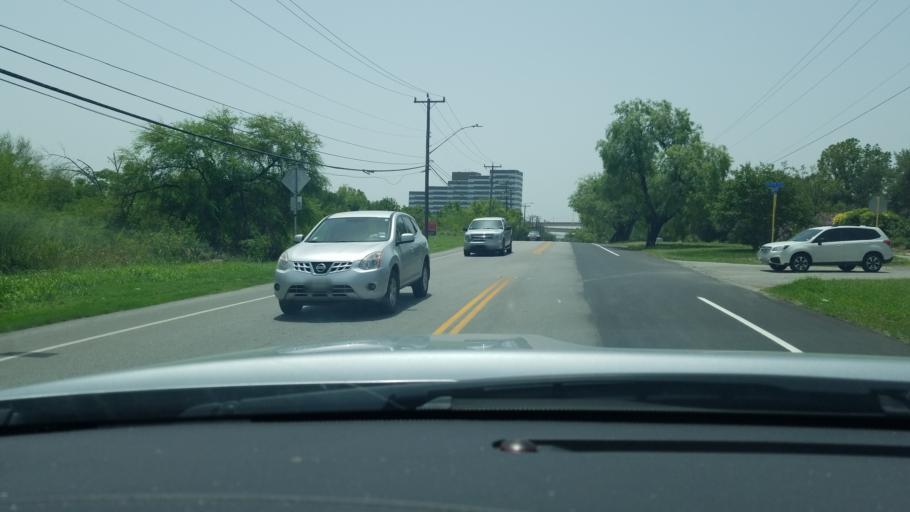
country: US
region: Texas
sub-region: Bexar County
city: Castle Hills
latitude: 29.5245
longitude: -98.4849
